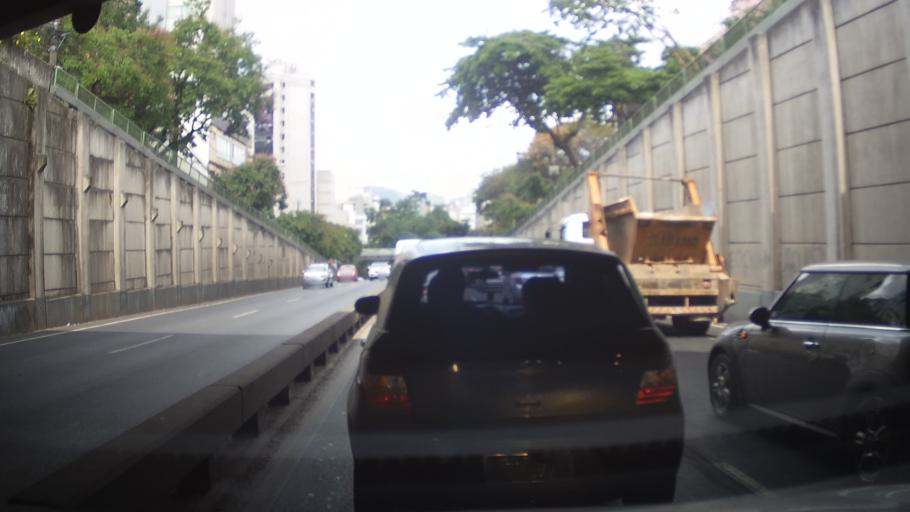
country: BR
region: Minas Gerais
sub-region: Belo Horizonte
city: Belo Horizonte
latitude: -19.9341
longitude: -43.9523
